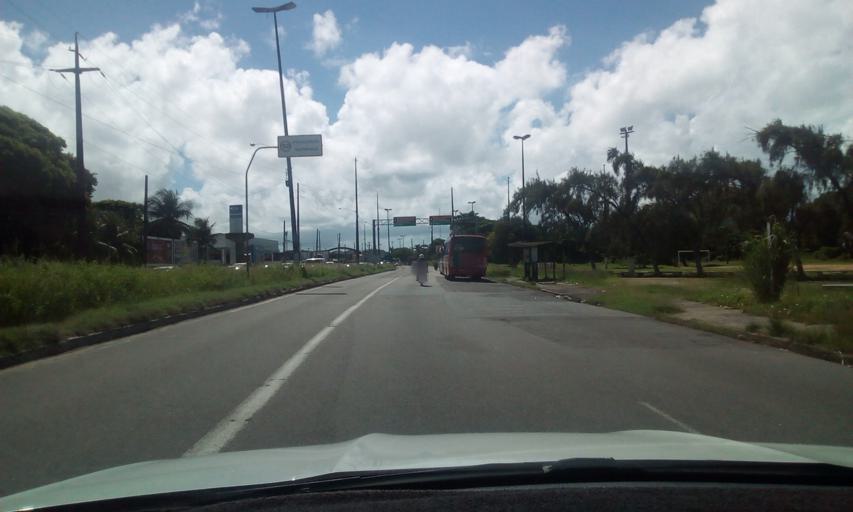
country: BR
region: Pernambuco
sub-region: Olinda
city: Olinda
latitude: -8.0263
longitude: -34.8643
